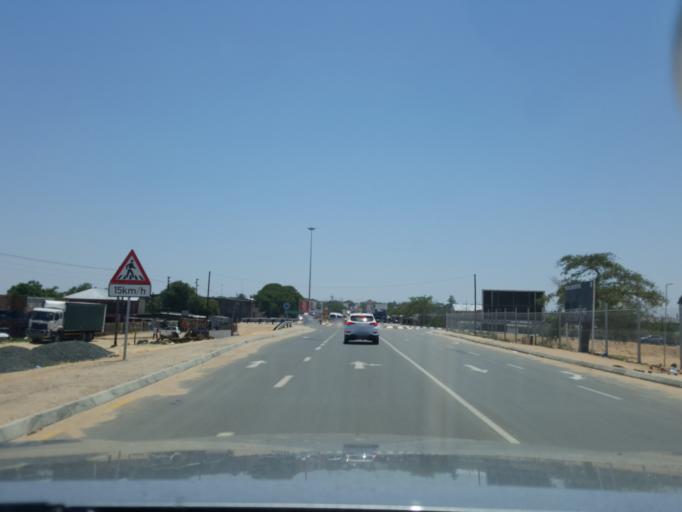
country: ZA
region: Limpopo
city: Thulamahashi
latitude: -24.6032
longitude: 31.0412
